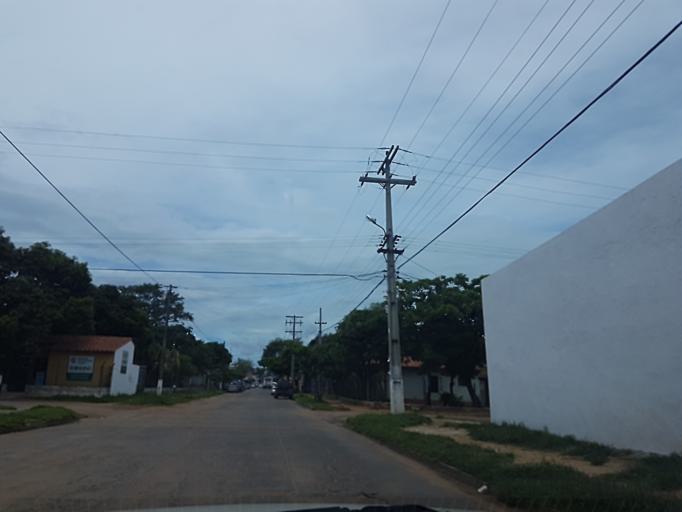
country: PY
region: Central
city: Limpio
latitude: -25.1705
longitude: -57.4776
